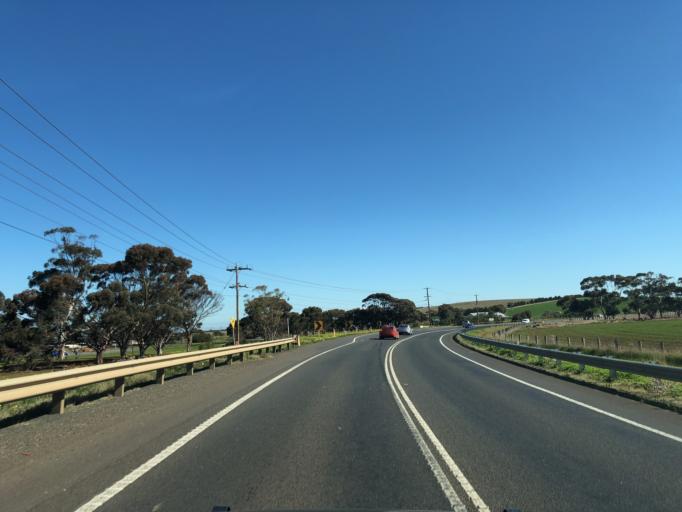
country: AU
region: Victoria
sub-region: Melton
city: Kurunjang
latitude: -37.6275
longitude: 144.6469
